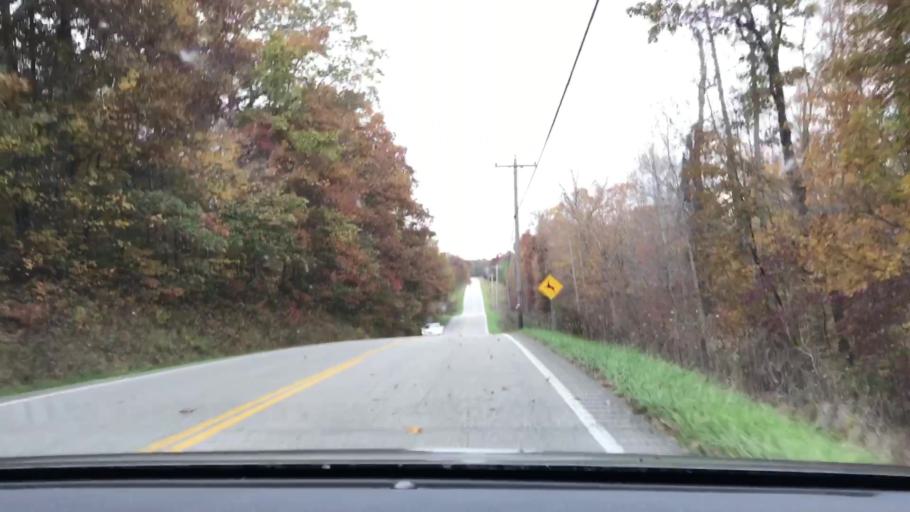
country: US
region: Tennessee
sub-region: Scott County
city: Huntsville
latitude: 36.3405
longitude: -84.6473
